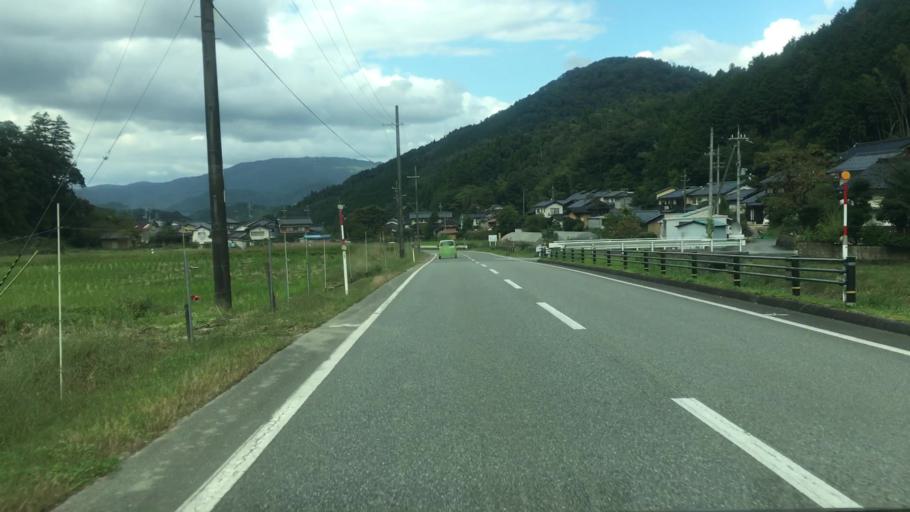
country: JP
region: Hyogo
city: Toyooka
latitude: 35.4338
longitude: 134.7353
